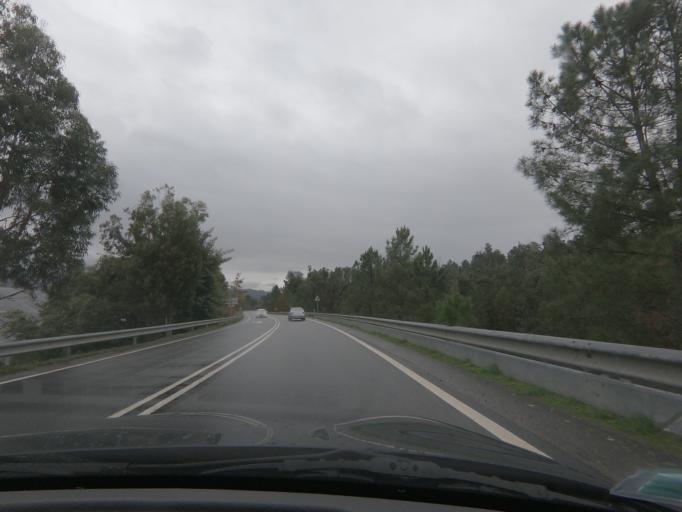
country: PT
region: Braga
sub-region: Celorico de Basto
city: Celorico de Basto
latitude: 41.3337
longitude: -8.0390
